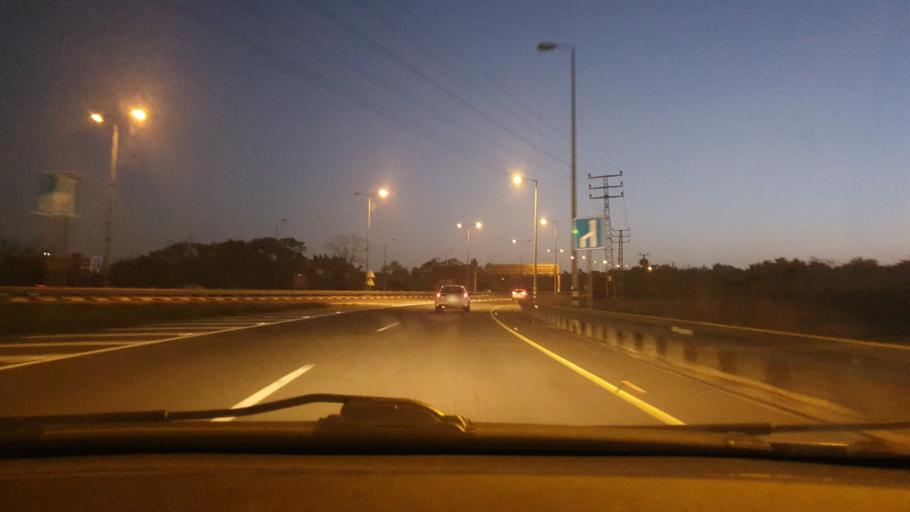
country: IL
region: Central District
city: Bet Dagan
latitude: 32.0003
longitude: 34.8196
